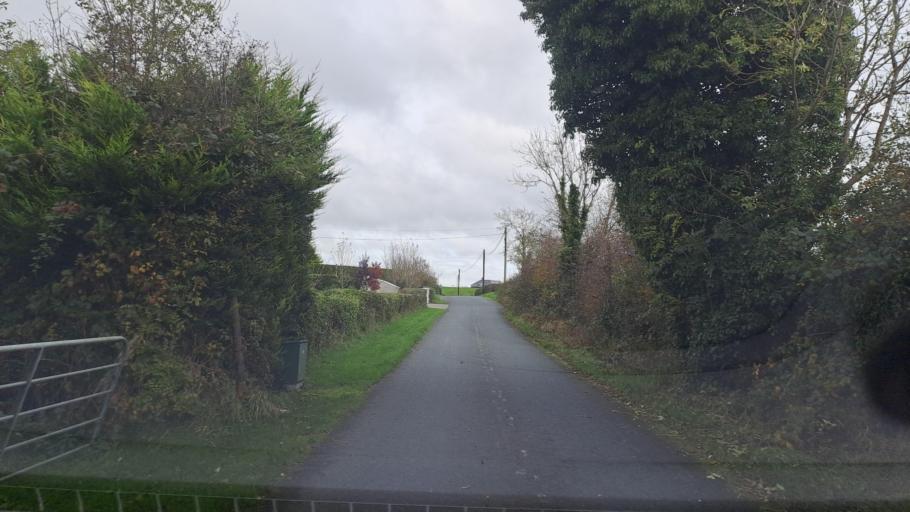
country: IE
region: Ulster
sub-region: An Cabhan
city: Bailieborough
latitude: 54.0128
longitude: -6.8904
